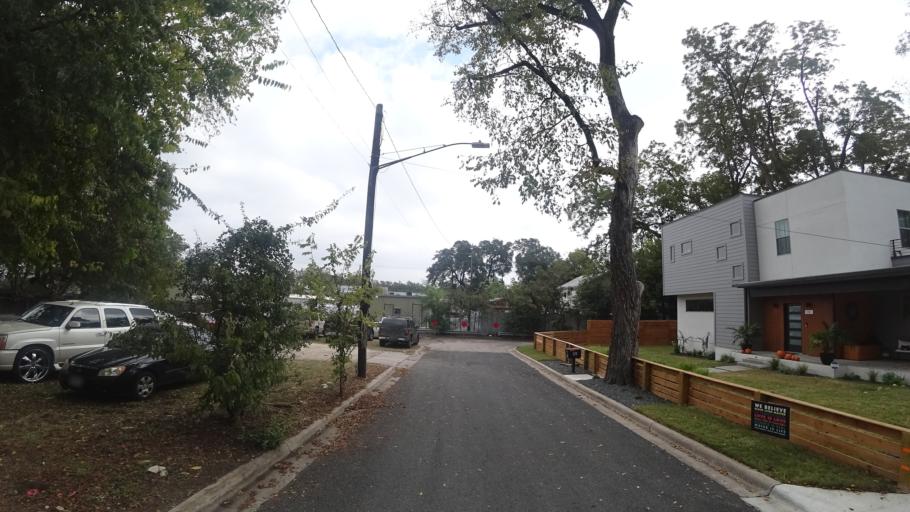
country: US
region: Texas
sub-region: Travis County
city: Austin
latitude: 30.2505
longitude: -97.7558
